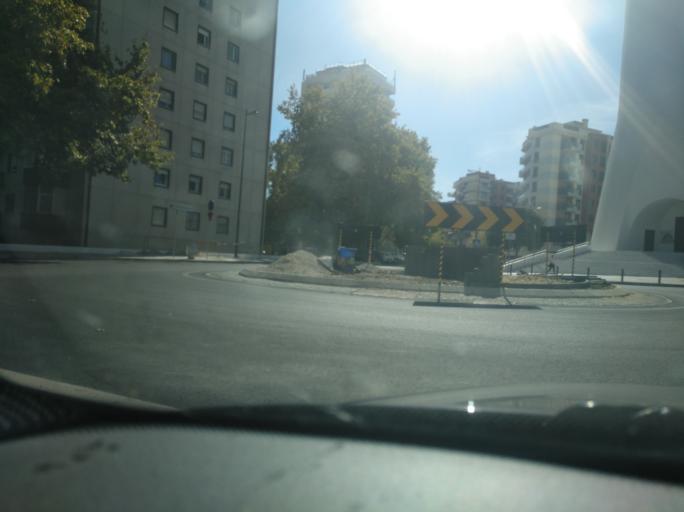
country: PT
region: Lisbon
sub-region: Oeiras
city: Alges
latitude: 38.7098
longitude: -9.2275
